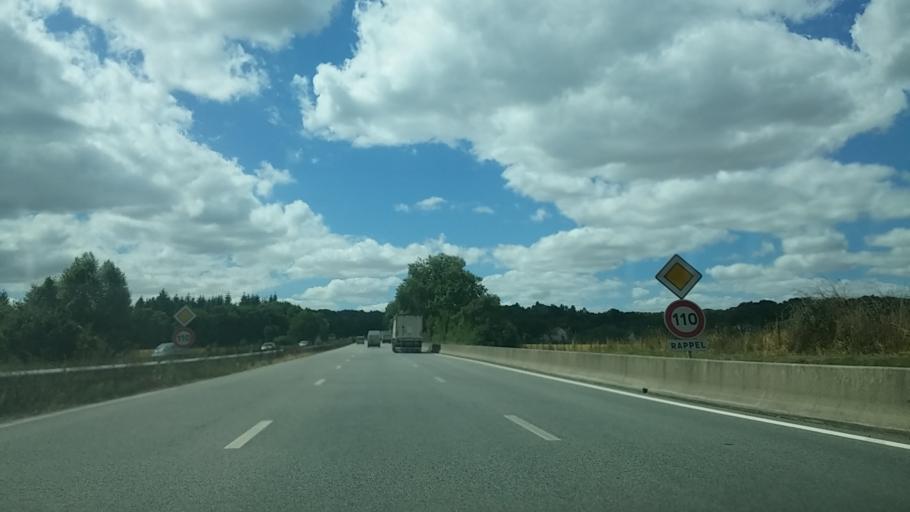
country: FR
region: Ile-de-France
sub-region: Departement des Yvelines
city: La Queue-les-Yvelines
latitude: 48.7991
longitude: 1.7756
